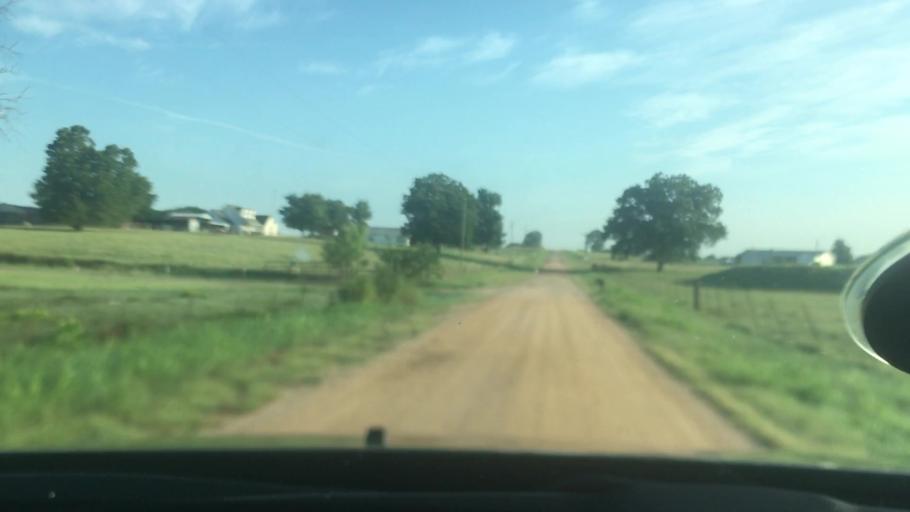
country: US
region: Oklahoma
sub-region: Pontotoc County
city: Ada
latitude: 34.8159
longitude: -96.7748
